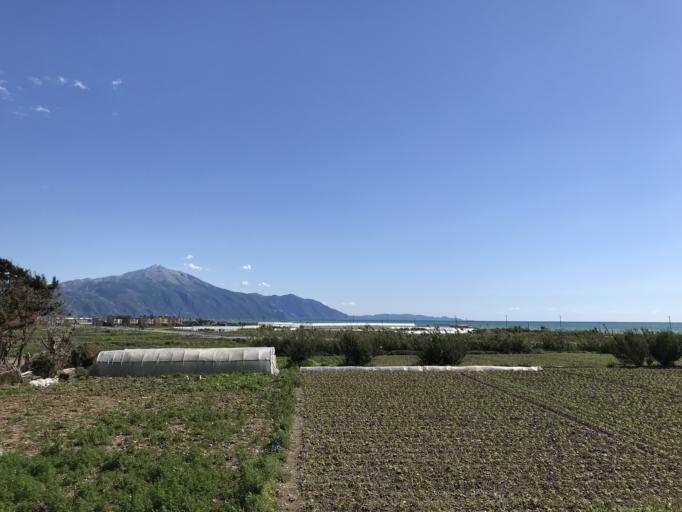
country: TR
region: Hatay
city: Samandag
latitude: 36.1138
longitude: 35.9306
